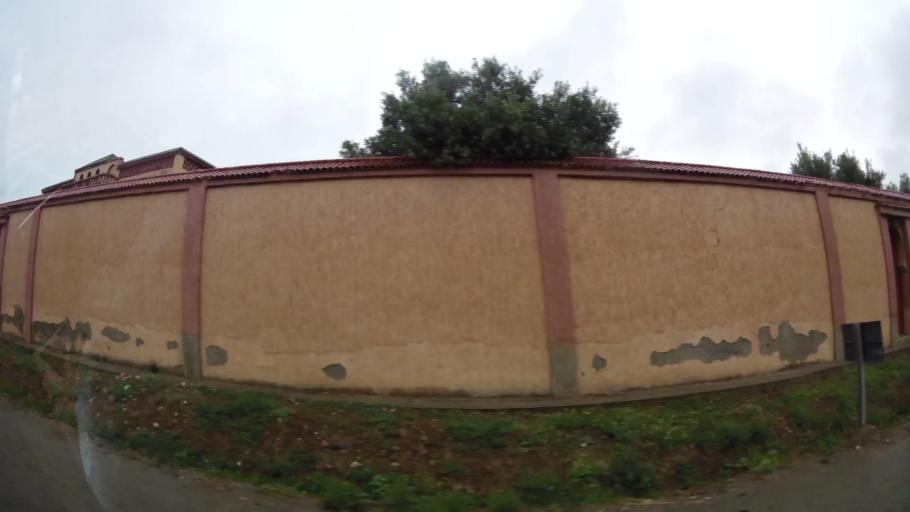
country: MA
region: Taza-Al Hoceima-Taounate
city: Imzourene
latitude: 35.1859
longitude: -3.8829
